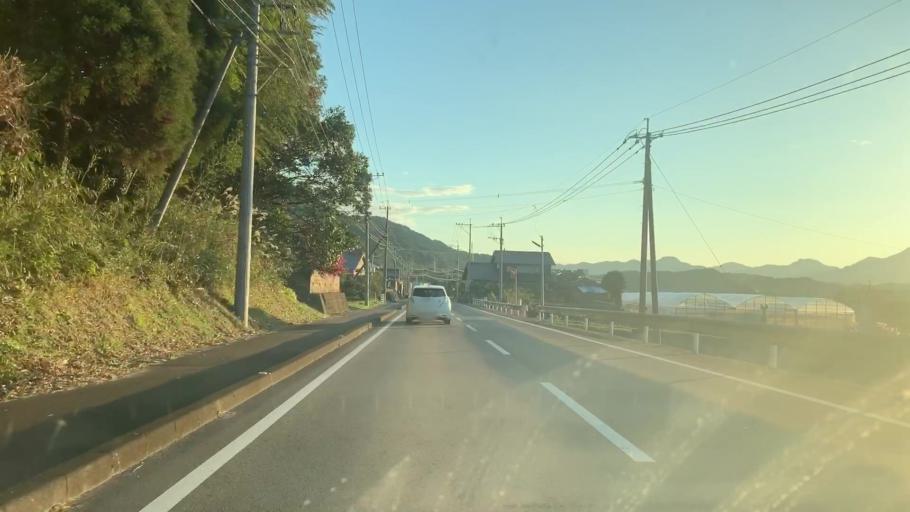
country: JP
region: Saga Prefecture
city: Imaricho-ko
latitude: 33.2861
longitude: 129.9701
